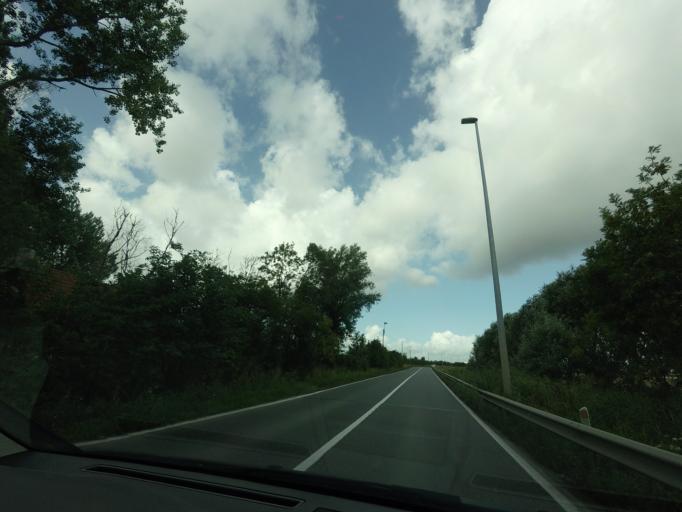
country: BE
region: Flanders
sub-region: Provincie West-Vlaanderen
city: Oudenburg
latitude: 51.2118
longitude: 3.0016
